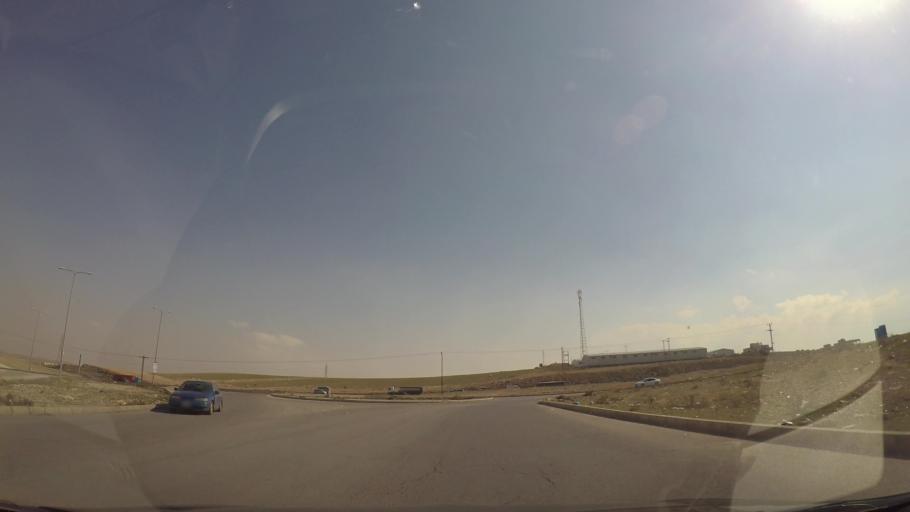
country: JO
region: Zarqa
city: Zarqa
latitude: 32.0470
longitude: 36.1170
